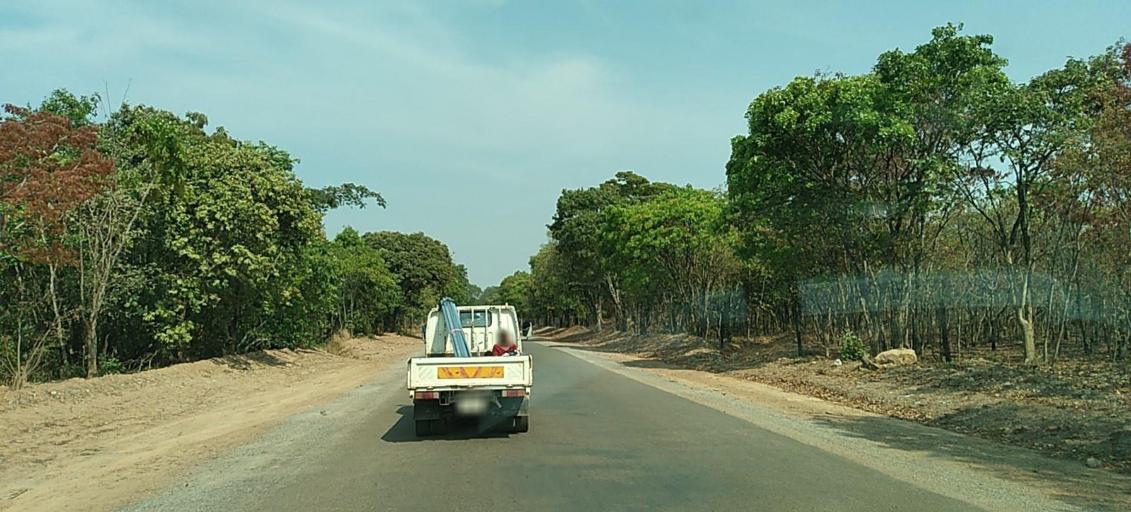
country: ZM
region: Copperbelt
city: Chililabombwe
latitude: -12.3061
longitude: 27.7872
